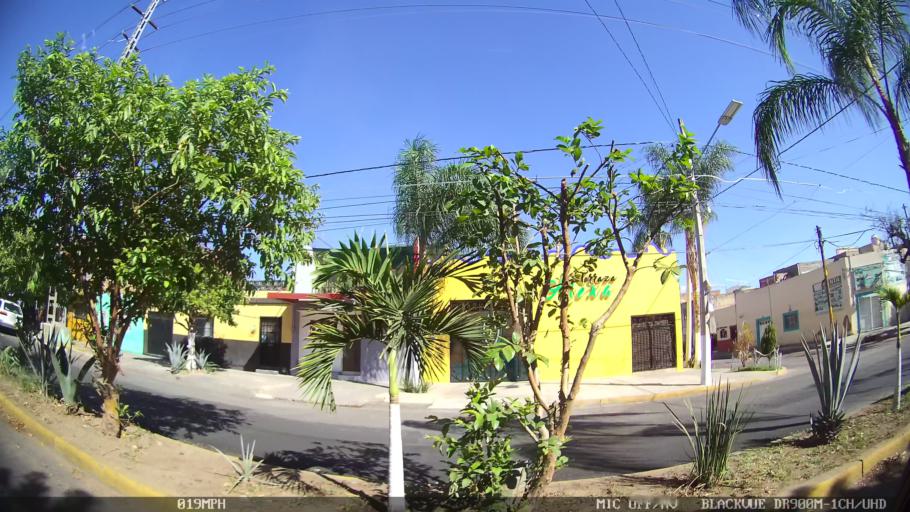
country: MX
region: Jalisco
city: Tlaquepaque
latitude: 20.6684
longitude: -103.2832
